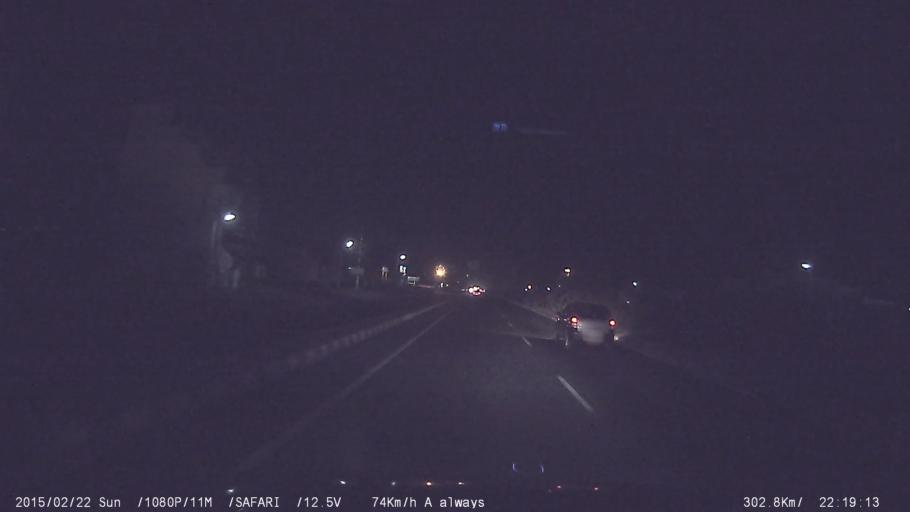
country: IN
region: Tamil Nadu
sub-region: Karur
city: Karur
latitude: 10.9775
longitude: 78.0637
